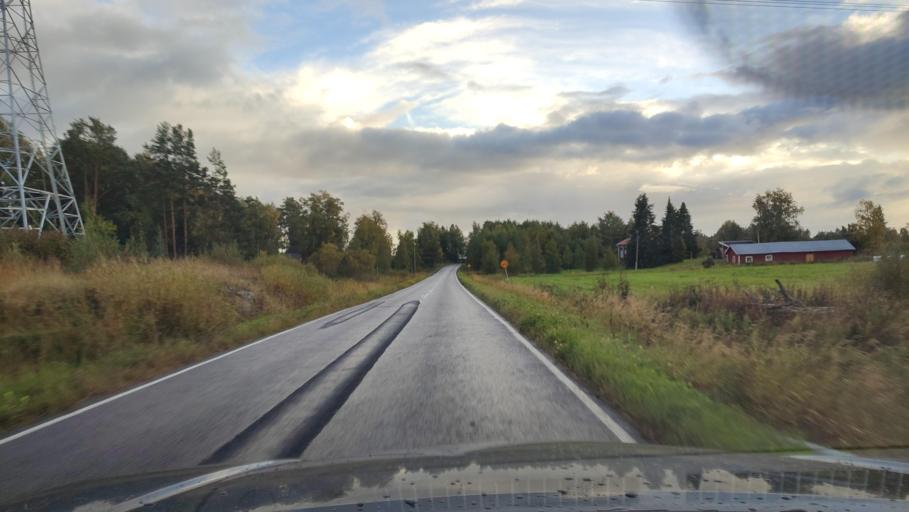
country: FI
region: Ostrobothnia
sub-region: Sydosterbotten
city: Kristinestad
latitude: 62.2868
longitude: 21.4221
